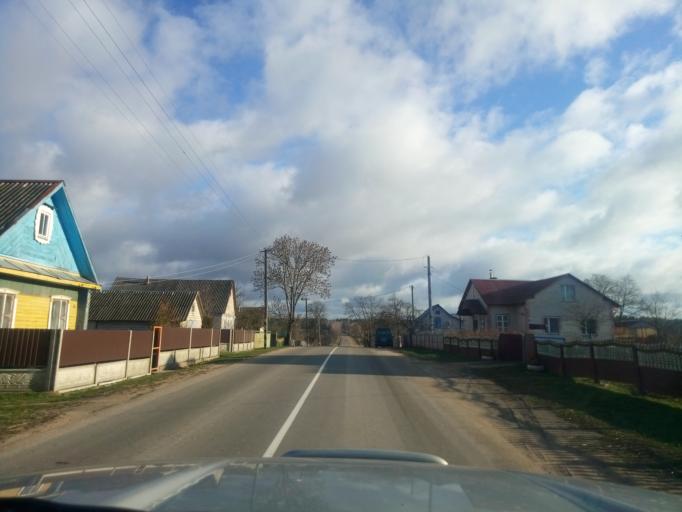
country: BY
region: Minsk
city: Tsimkavichy
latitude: 53.1754
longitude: 26.9637
